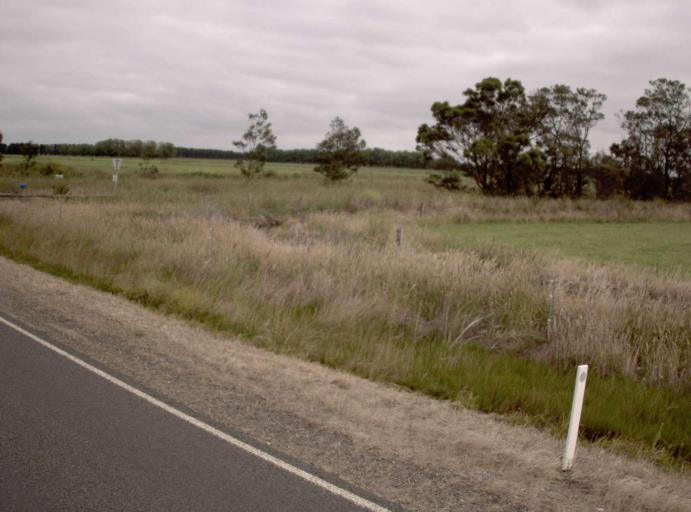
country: AU
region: Victoria
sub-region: Wellington
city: Sale
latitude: -38.0601
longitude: 146.9698
